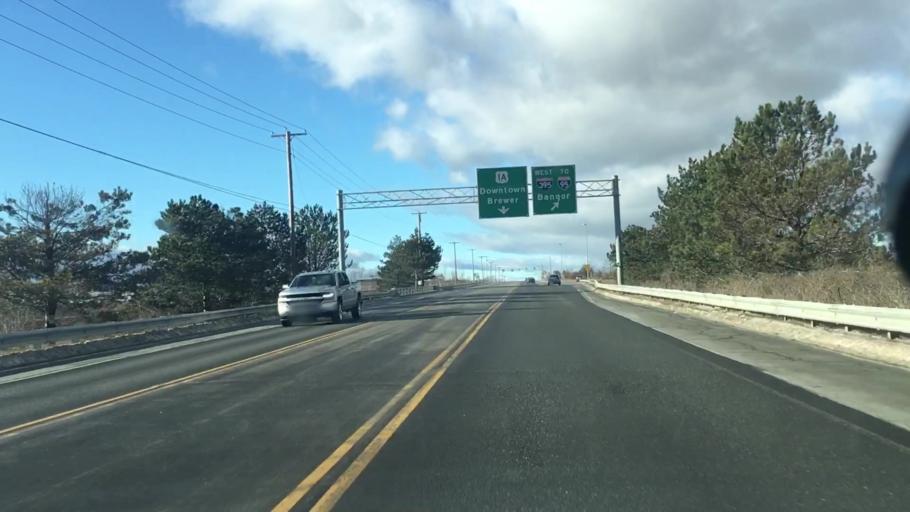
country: US
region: Maine
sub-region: Penobscot County
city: Holden
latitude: 44.7709
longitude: -68.7206
